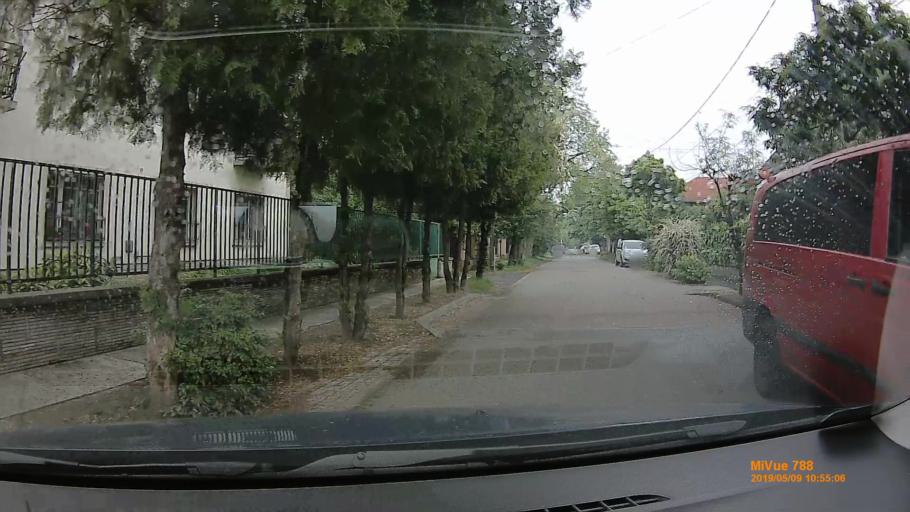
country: HU
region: Budapest
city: Budapest XVI. keruelet
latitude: 47.5206
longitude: 19.1619
